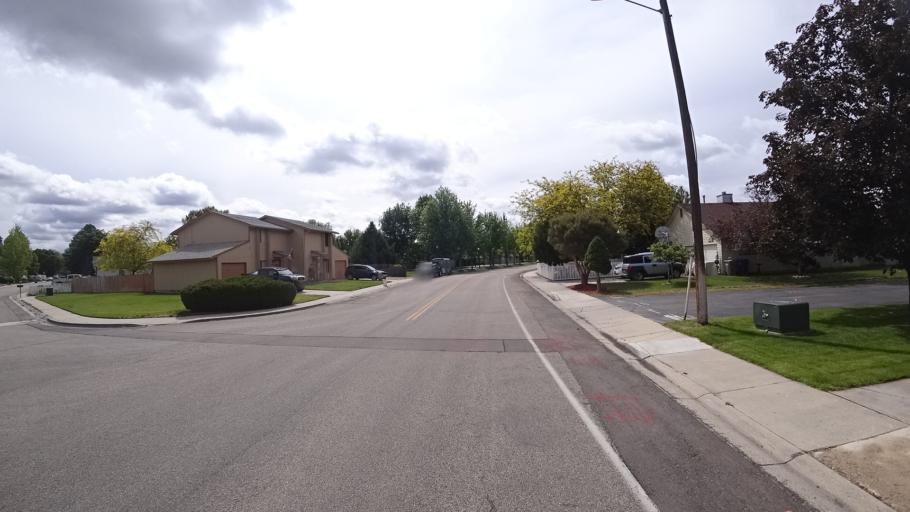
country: US
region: Idaho
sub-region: Ada County
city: Eagle
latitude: 43.6970
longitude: -116.3480
